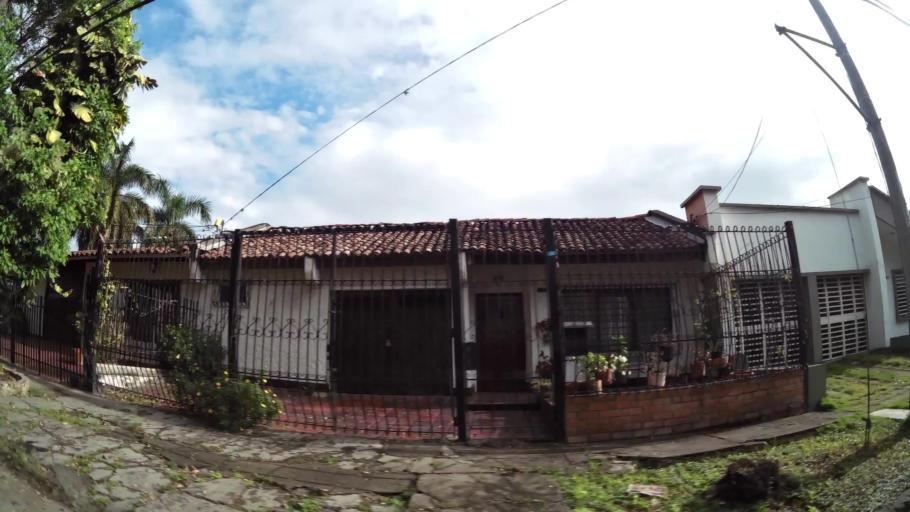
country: CO
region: Valle del Cauca
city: Cali
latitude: 3.4861
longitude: -76.5217
